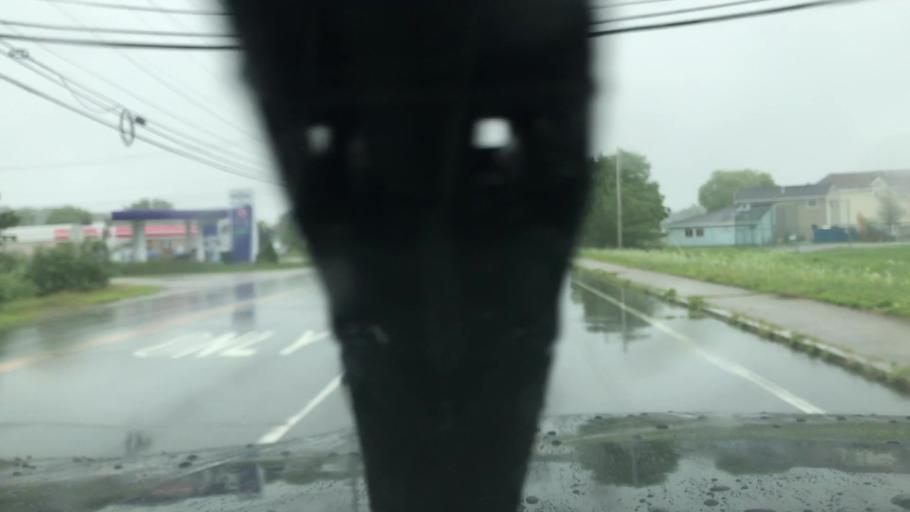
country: US
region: New Hampshire
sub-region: Strafford County
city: Madbury
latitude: 43.1783
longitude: -70.9028
